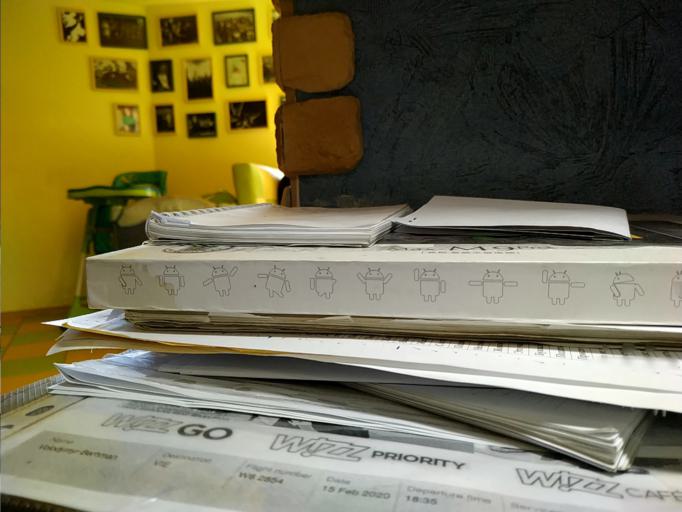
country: RU
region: Pskov
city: Plyussa
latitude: 58.4488
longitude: 29.6253
